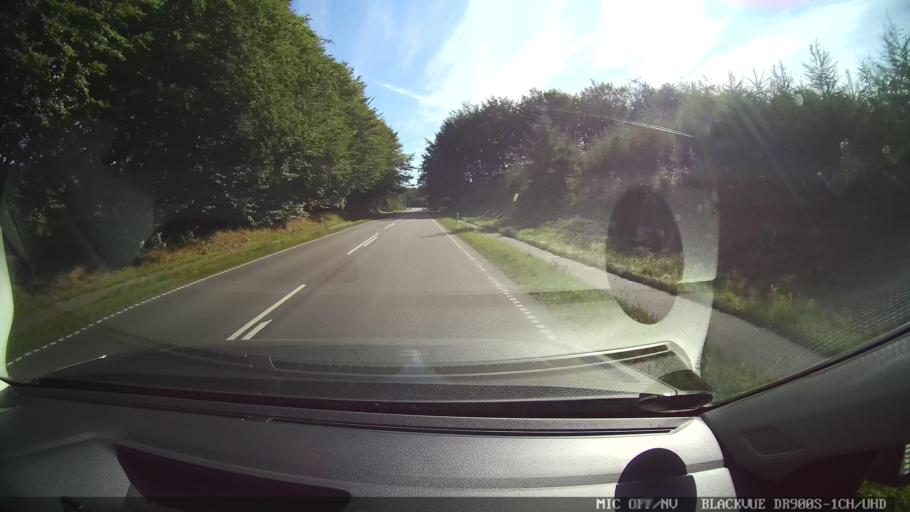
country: DK
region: North Denmark
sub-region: Mariagerfjord Kommune
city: Arden
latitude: 56.7738
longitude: 9.7843
